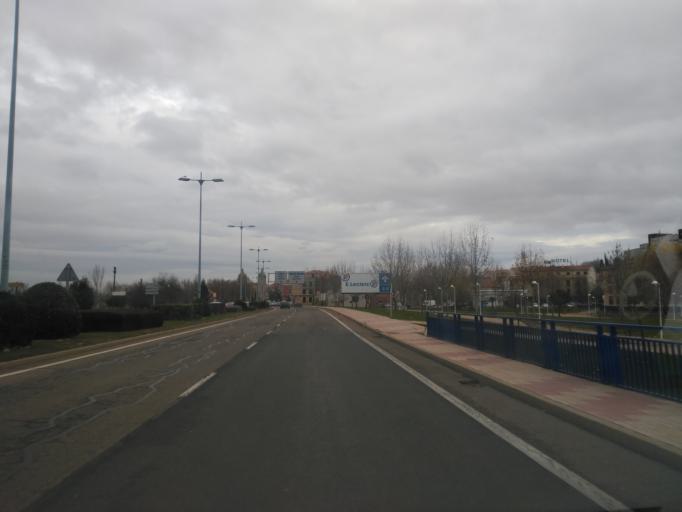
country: ES
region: Castille and Leon
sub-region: Provincia de Salamanca
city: Salamanca
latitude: 40.9573
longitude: -5.6743
